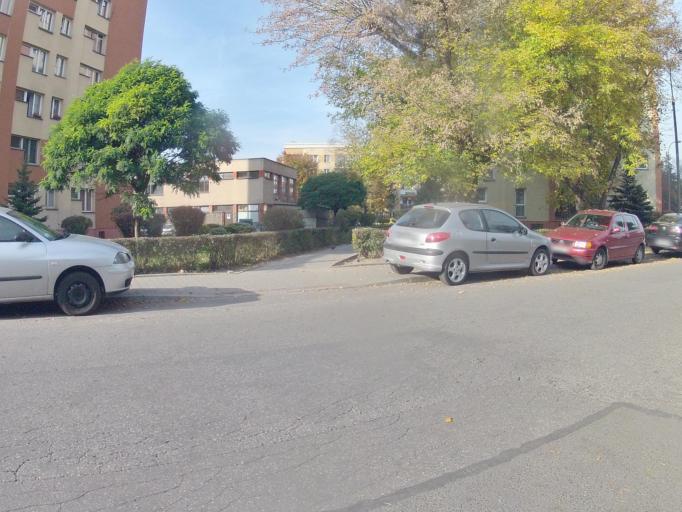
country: PL
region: Lesser Poland Voivodeship
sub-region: Krakow
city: Krakow
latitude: 50.0578
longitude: 19.9805
